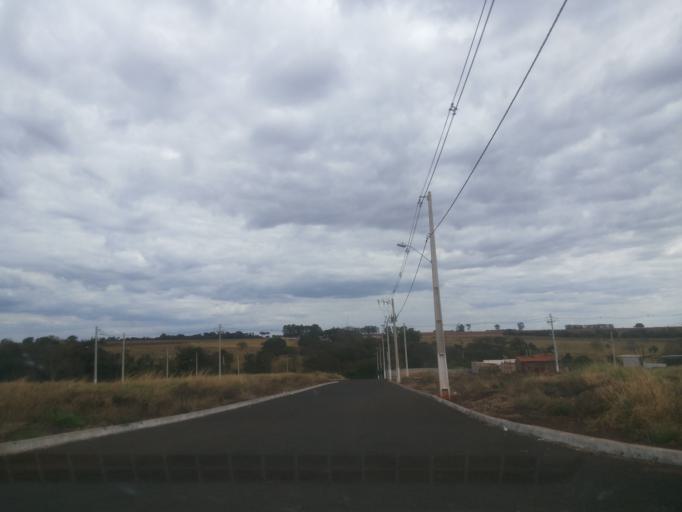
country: BR
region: Minas Gerais
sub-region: Centralina
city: Centralina
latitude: -18.7312
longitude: -49.2015
